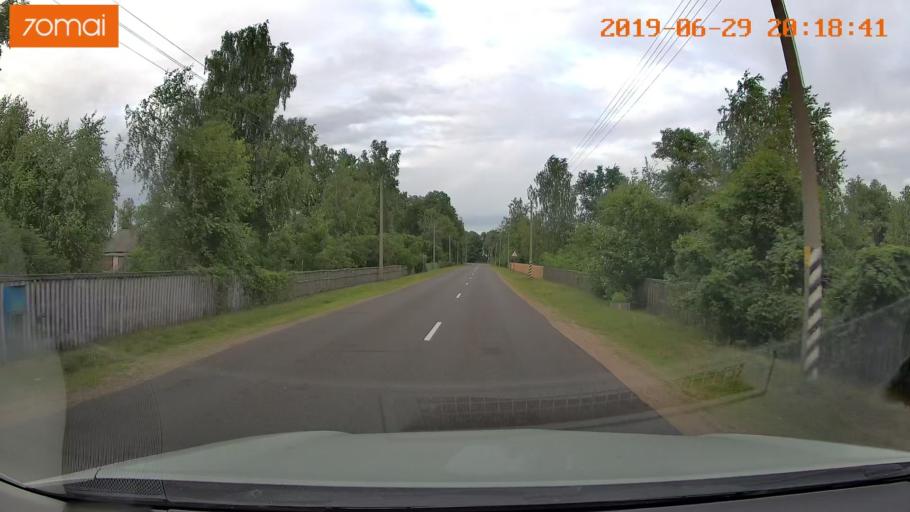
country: BY
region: Brest
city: Asnyezhytsy
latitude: 52.3957
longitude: 26.2385
